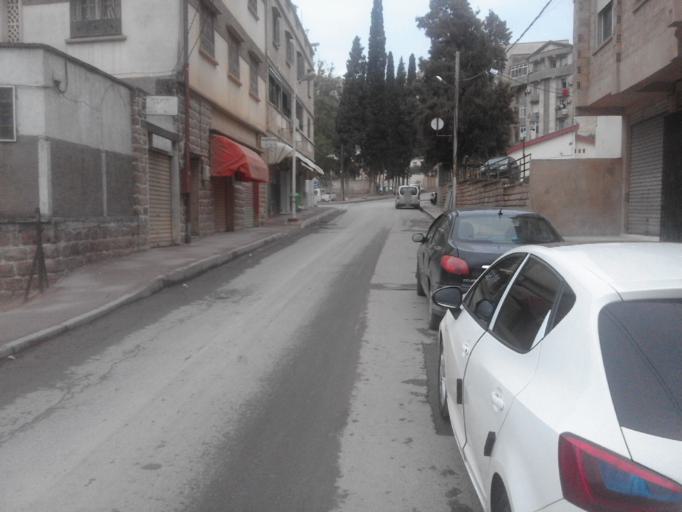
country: DZ
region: Bejaia
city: Seddouk
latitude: 36.6078
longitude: 4.6905
